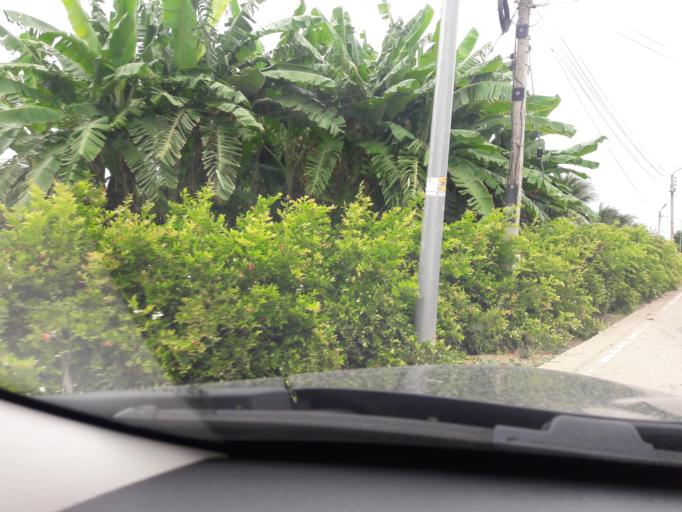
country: TH
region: Ratchaburi
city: Bang Phae
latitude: 13.6076
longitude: 99.9086
